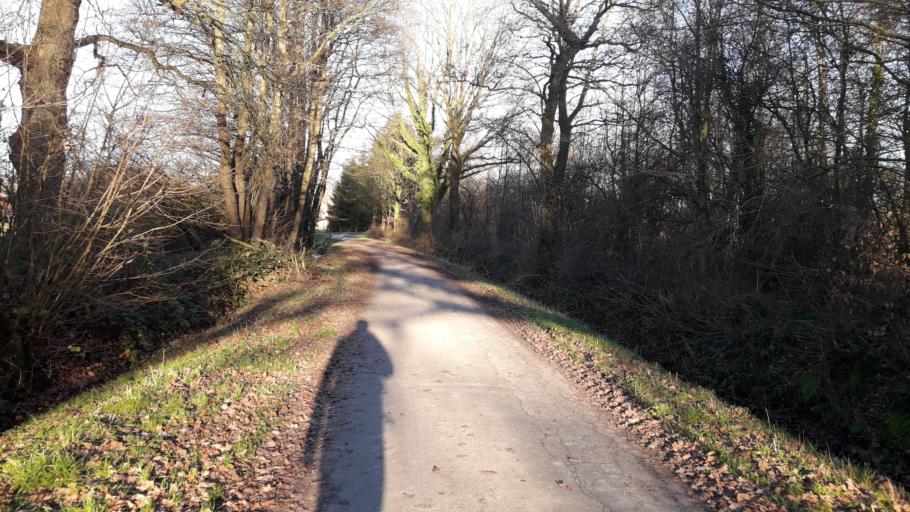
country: DE
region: Schleswig-Holstein
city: Quickborn
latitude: 53.7187
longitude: 9.8634
